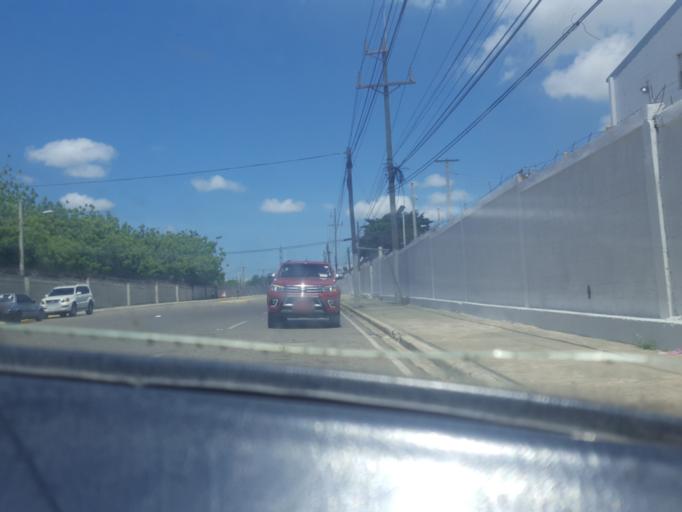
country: DO
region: Santiago
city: Santiago de los Caballeros
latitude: 19.4735
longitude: -70.7323
